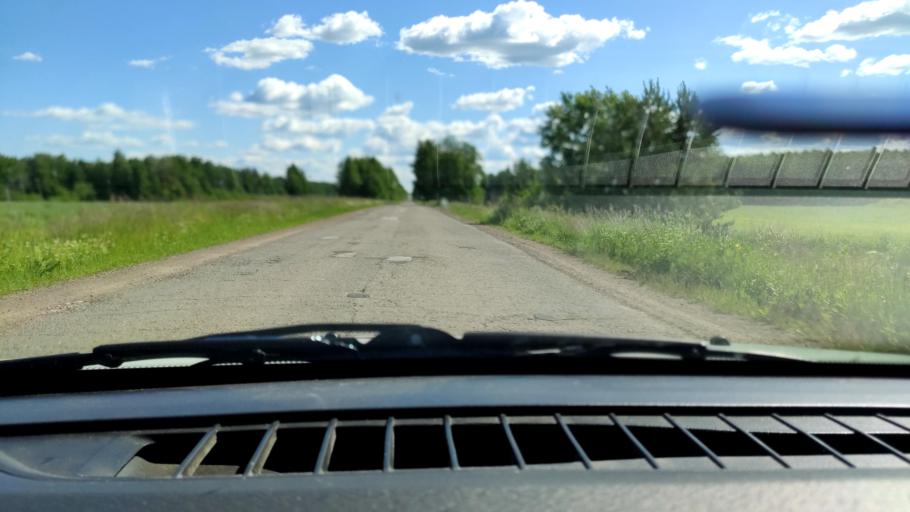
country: RU
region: Perm
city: Kukushtan
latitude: 57.2871
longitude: 56.5360
